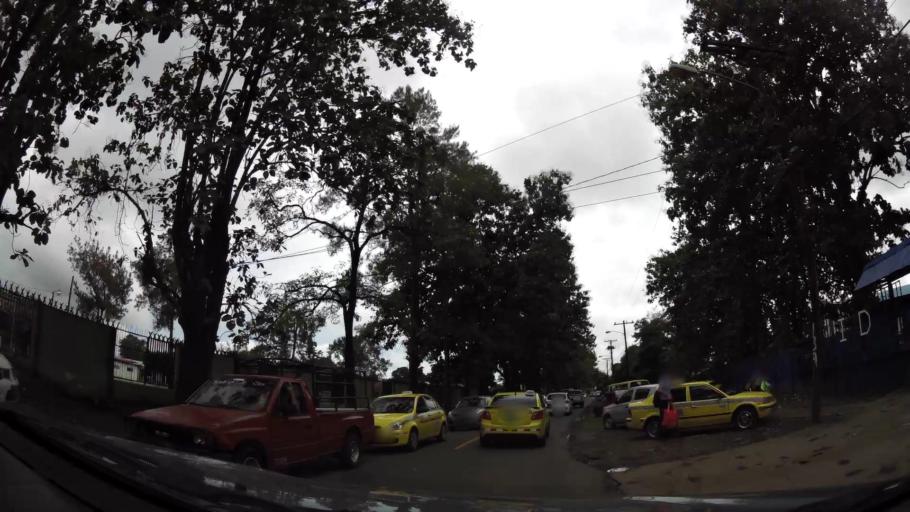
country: PA
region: Chiriqui
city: David
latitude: 8.4211
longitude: -82.4393
